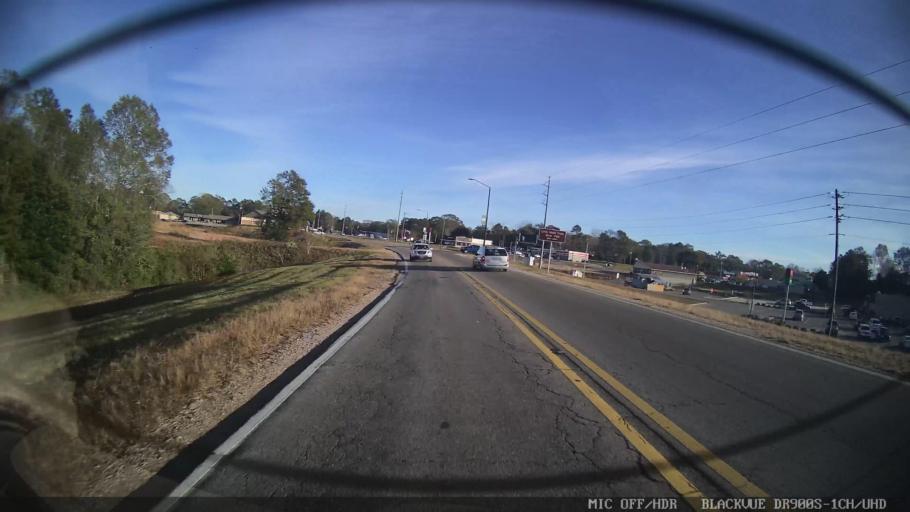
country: US
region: Mississippi
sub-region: Lamar County
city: Purvis
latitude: 31.1473
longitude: -89.4047
